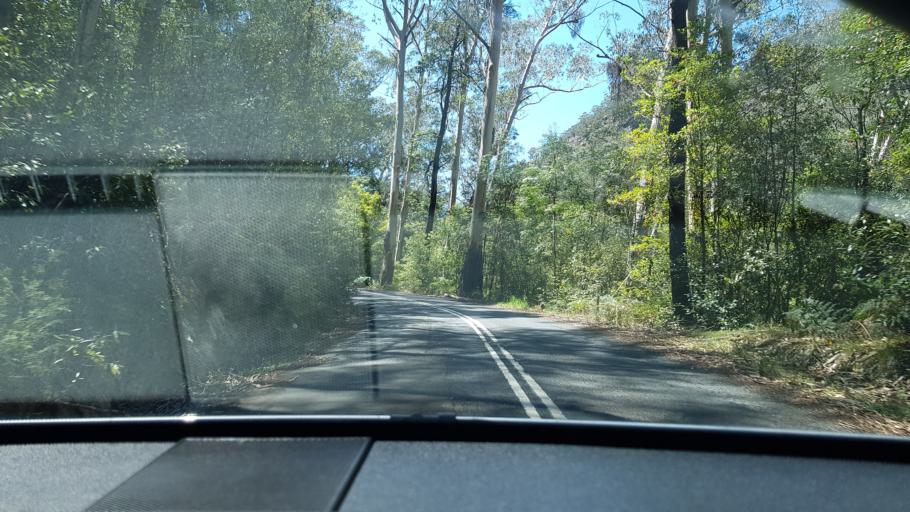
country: AU
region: New South Wales
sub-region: Blue Mountains Municipality
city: Blackheath
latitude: -33.6642
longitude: 150.2713
